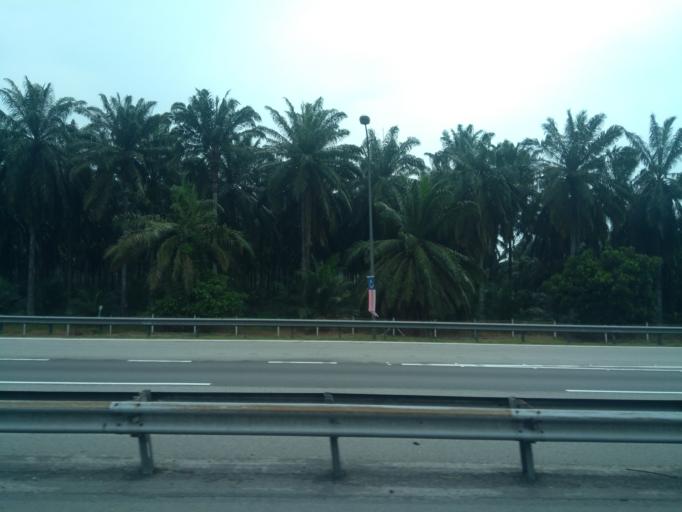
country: MY
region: Perak
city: Taiping
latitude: 4.8265
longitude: 100.6756
